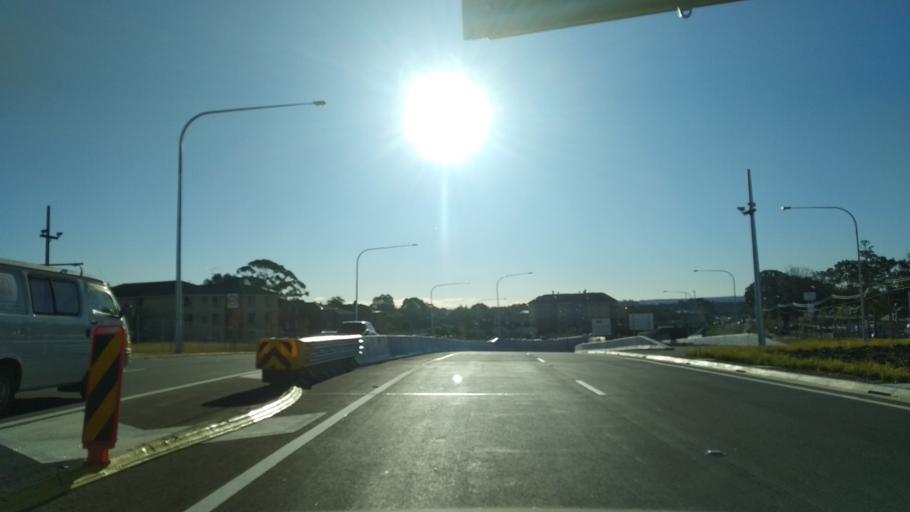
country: AU
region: New South Wales
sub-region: Ashfield
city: Summer Hill
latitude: -33.8840
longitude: 151.1343
